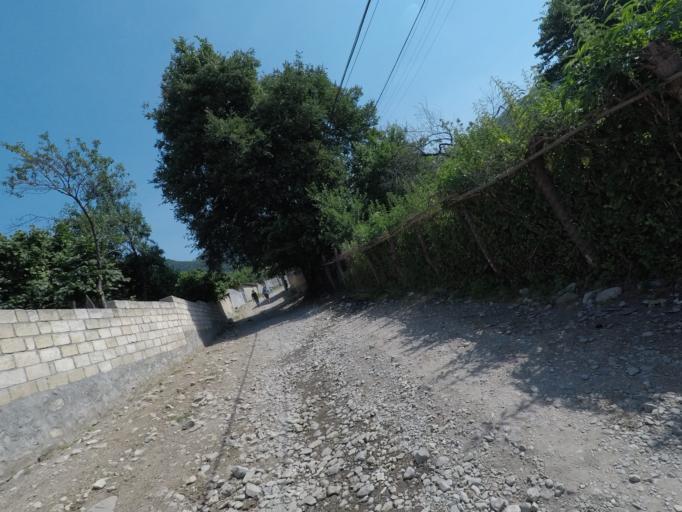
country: AZ
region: Qakh Rayon
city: Cinarli
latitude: 41.4834
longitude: 46.8492
